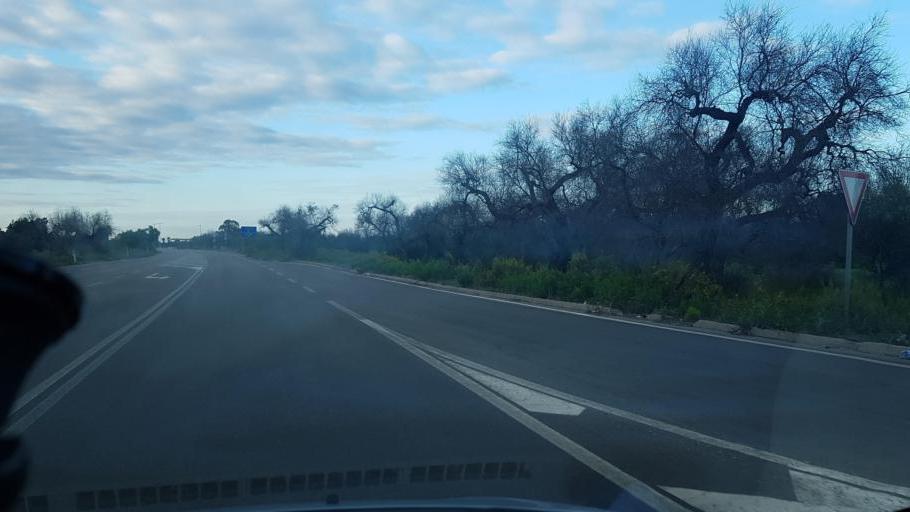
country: IT
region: Apulia
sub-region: Provincia di Lecce
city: Veglie
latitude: 40.3362
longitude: 17.9817
